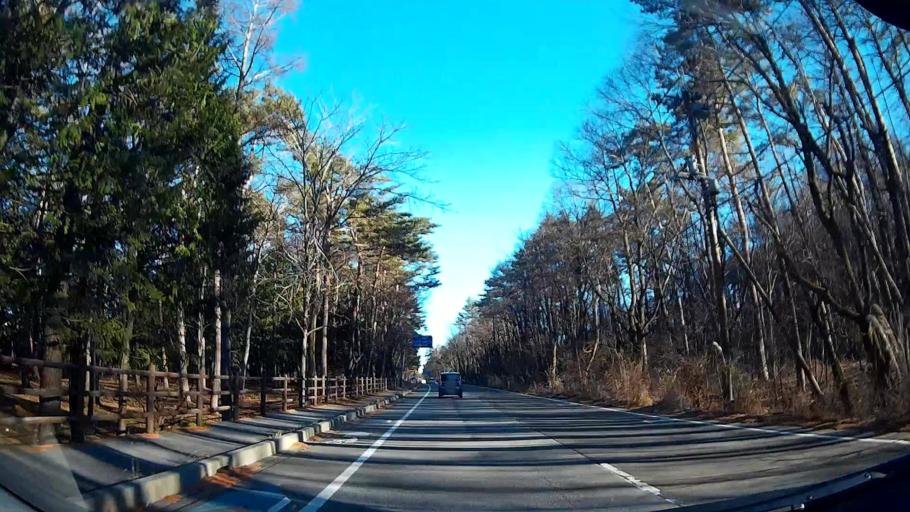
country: JP
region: Yamanashi
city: Fujikawaguchiko
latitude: 35.4452
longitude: 138.8247
